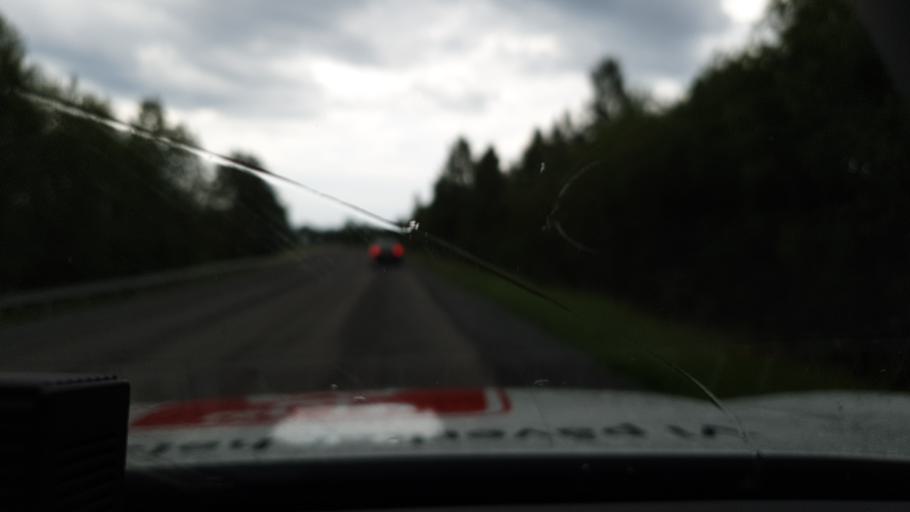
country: SE
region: Norrbotten
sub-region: Bodens Kommun
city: Boden
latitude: 65.8534
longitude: 21.4884
